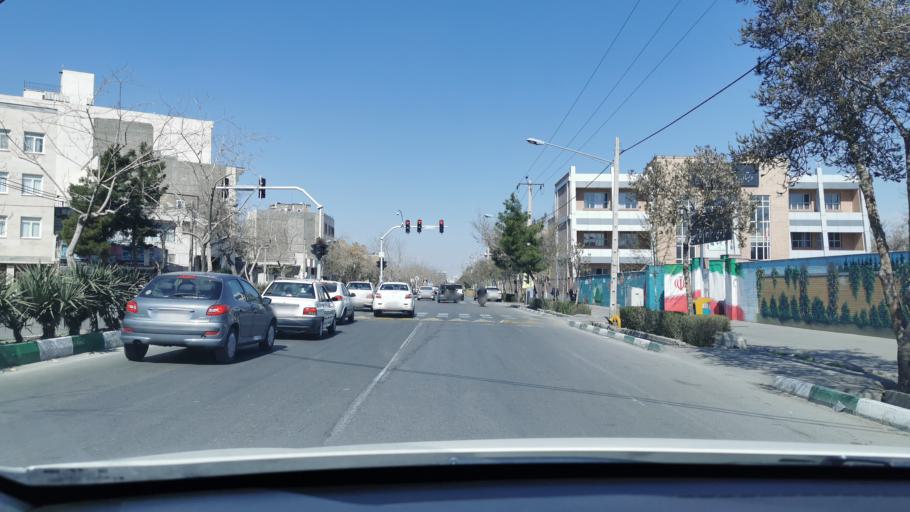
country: IR
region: Razavi Khorasan
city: Mashhad
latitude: 36.2763
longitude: 59.5765
